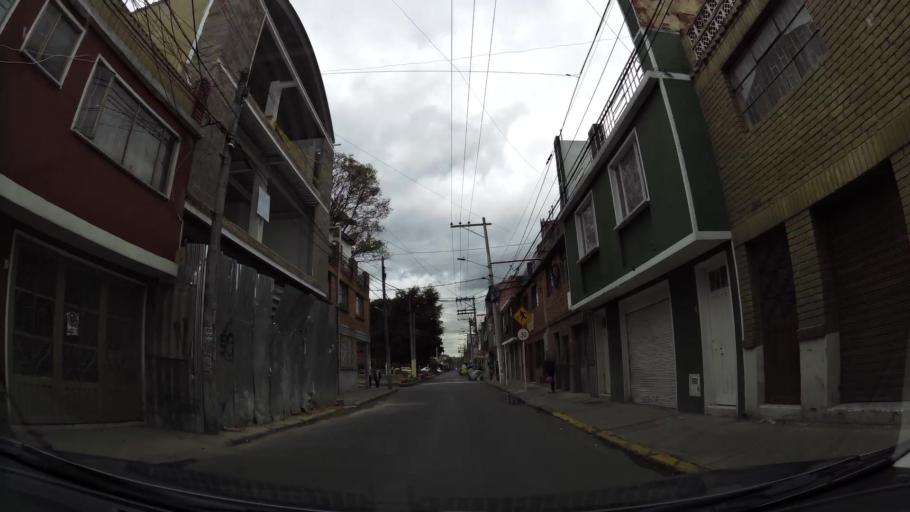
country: CO
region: Bogota D.C.
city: Bogota
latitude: 4.6803
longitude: -74.0923
